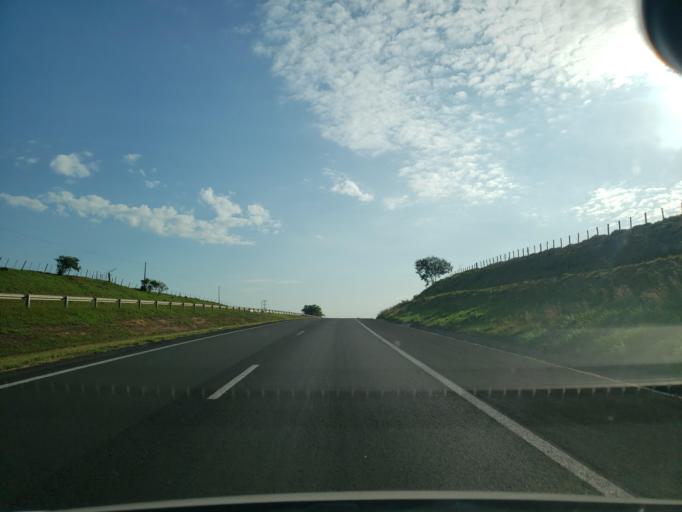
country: BR
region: Sao Paulo
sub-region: Valparaiso
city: Valparaiso
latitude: -21.2171
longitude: -50.8477
